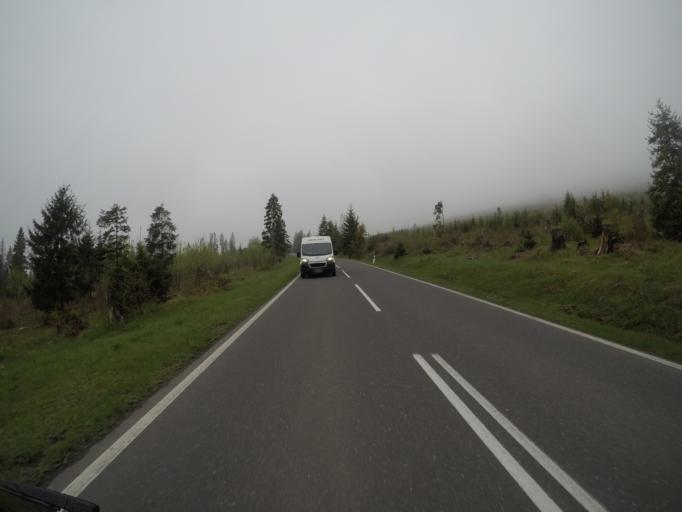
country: SK
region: Presovsky
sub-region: Okres Poprad
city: Strba
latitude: 49.0996
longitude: 20.0660
